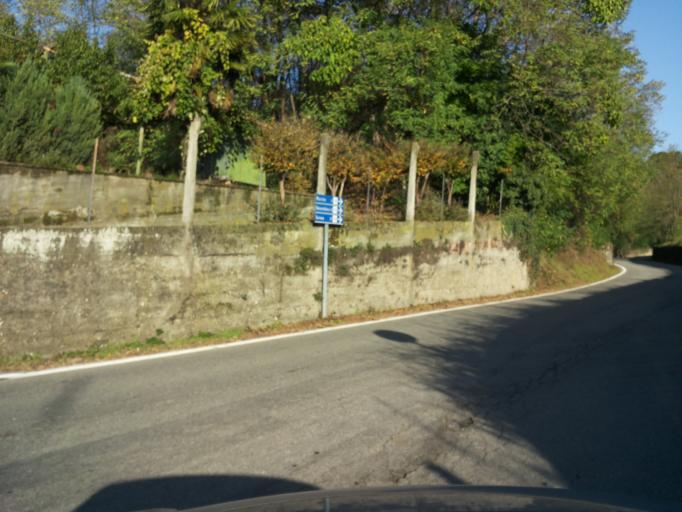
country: IT
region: Piedmont
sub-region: Provincia di Torino
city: Mazze
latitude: 45.3040
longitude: 7.9341
